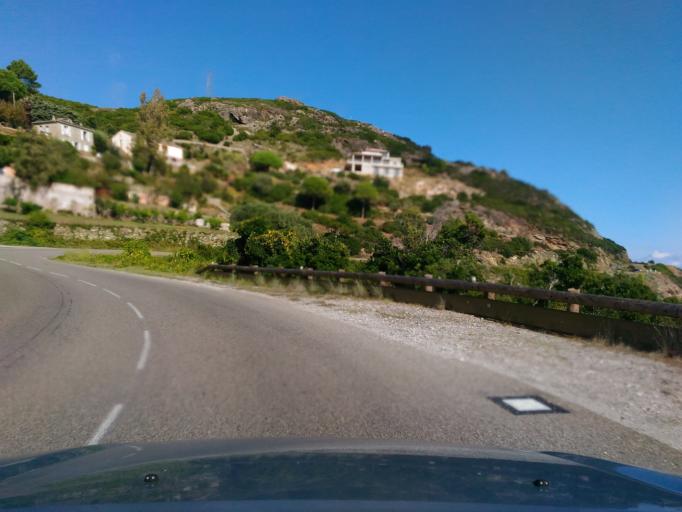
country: FR
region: Corsica
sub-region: Departement de la Haute-Corse
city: Brando
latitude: 42.7946
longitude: 9.4892
